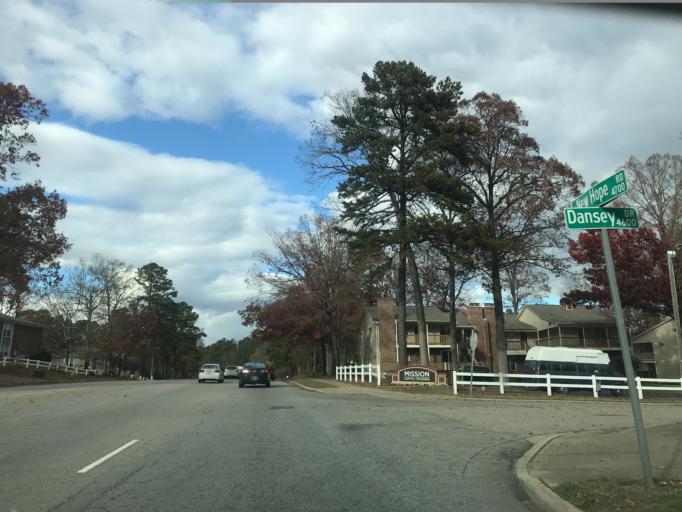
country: US
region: North Carolina
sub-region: Wake County
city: Raleigh
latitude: 35.8457
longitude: -78.5743
